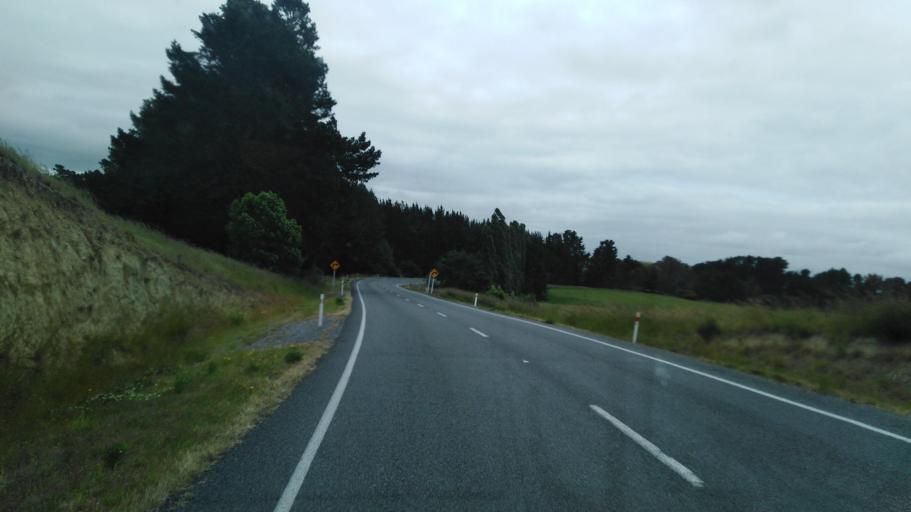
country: NZ
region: Canterbury
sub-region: Kaikoura District
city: Kaikoura
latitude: -42.7745
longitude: 173.2737
